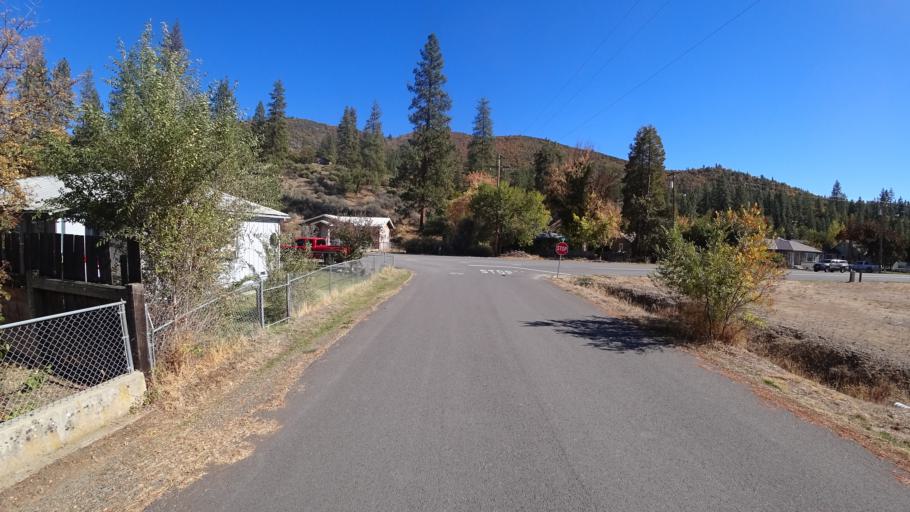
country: US
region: California
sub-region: Siskiyou County
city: Yreka
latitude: 41.6125
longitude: -122.8388
